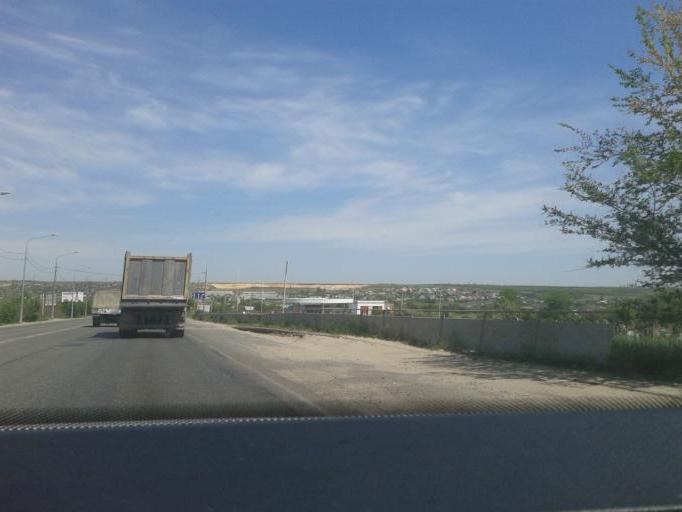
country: RU
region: Volgograd
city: Gorodishche
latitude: 48.7866
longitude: 44.5204
